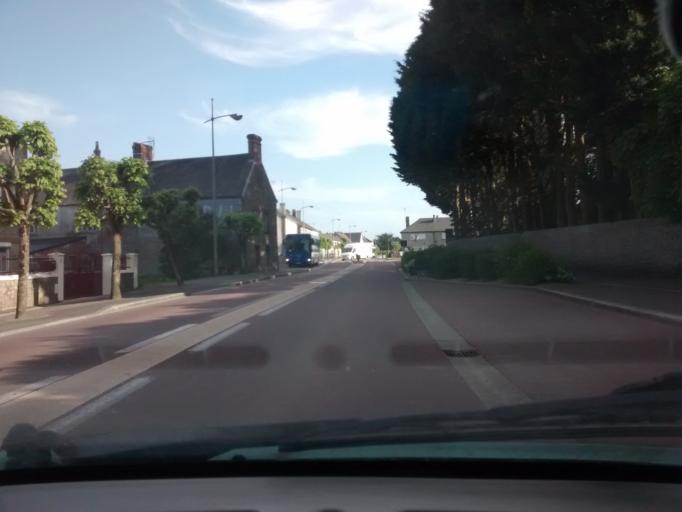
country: FR
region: Lower Normandy
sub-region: Departement de la Manche
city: Lessay
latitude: 49.2210
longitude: -1.5318
